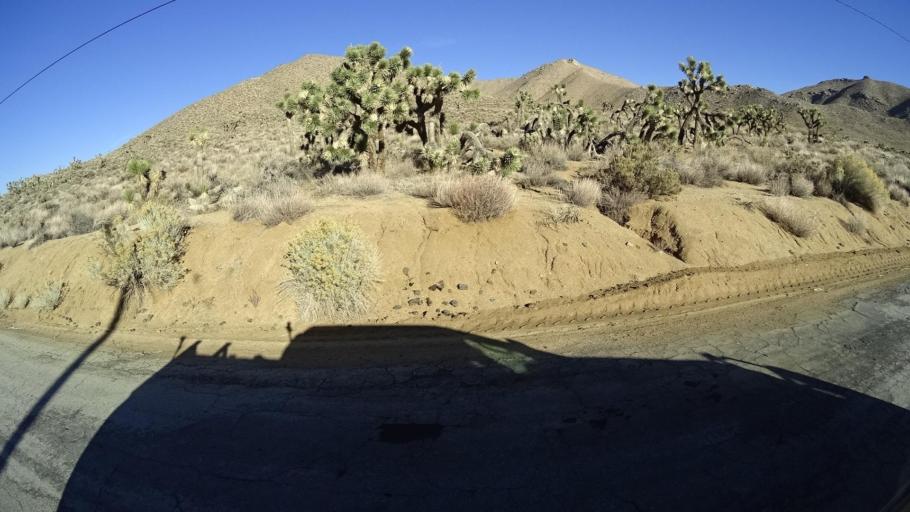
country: US
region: California
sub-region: Kern County
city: Weldon
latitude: 35.5282
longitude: -118.2009
